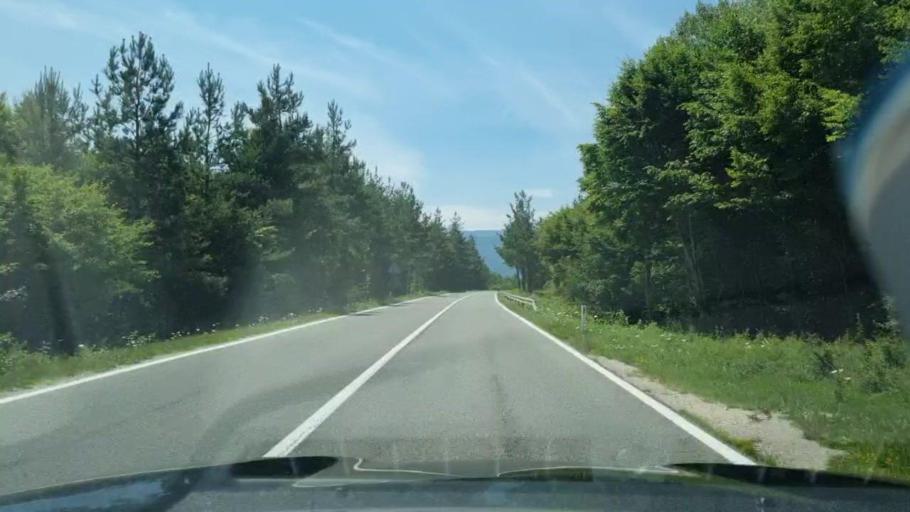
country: BA
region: Federation of Bosnia and Herzegovina
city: Sanica
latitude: 44.5443
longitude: 16.4154
